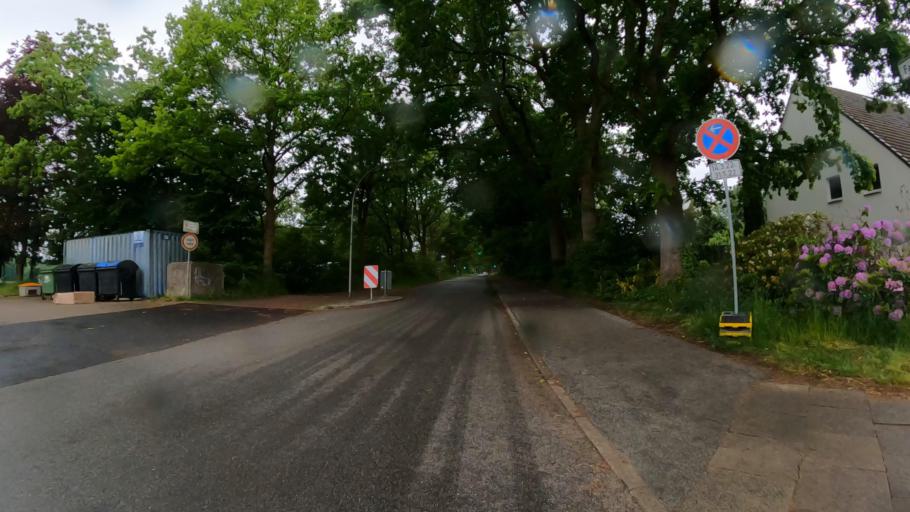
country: DE
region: Schleswig-Holstein
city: Norderstedt
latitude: 53.7018
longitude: 10.0055
